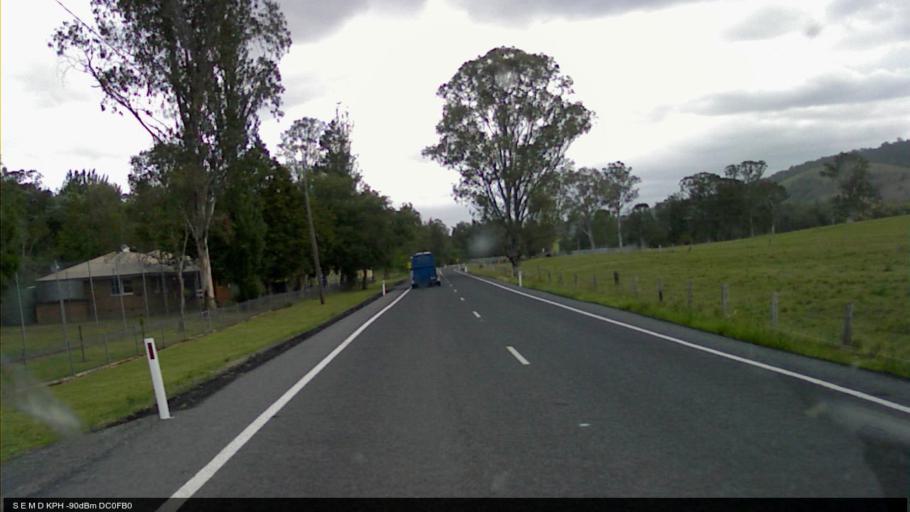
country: AU
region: New South Wales
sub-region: Gloucester Shire
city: Gloucester
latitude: -31.8974
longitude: 151.8801
